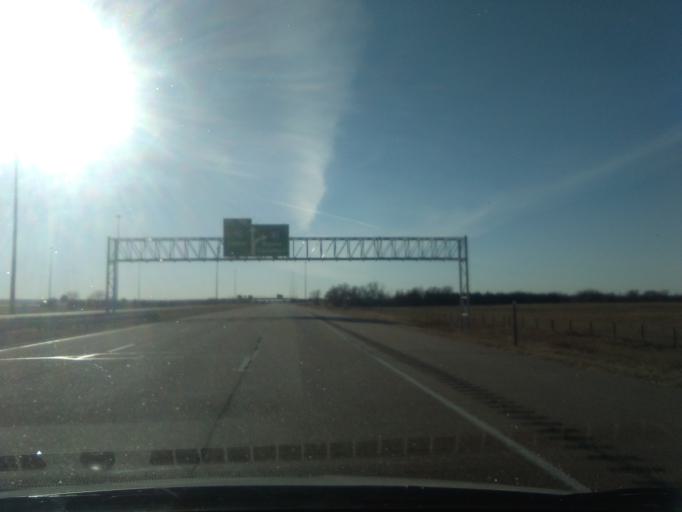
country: US
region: Colorado
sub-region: Sedgwick County
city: Julesburg
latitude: 41.0326
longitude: -102.1450
